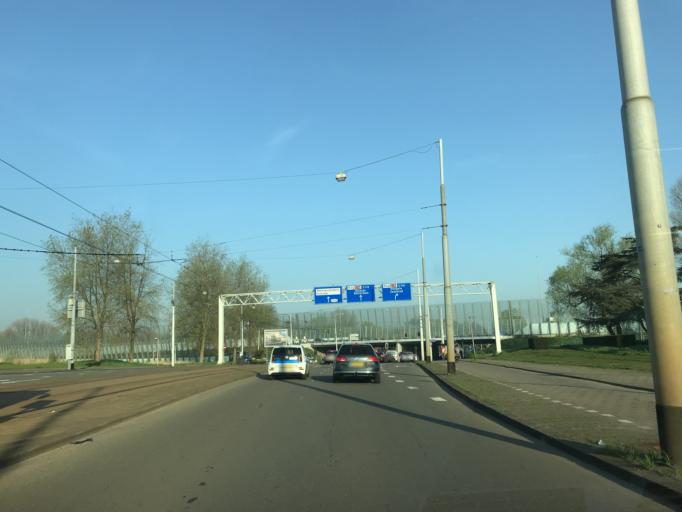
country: NL
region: North Holland
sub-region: Gemeente Diemen
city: Diemen
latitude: 52.3397
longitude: 4.9546
